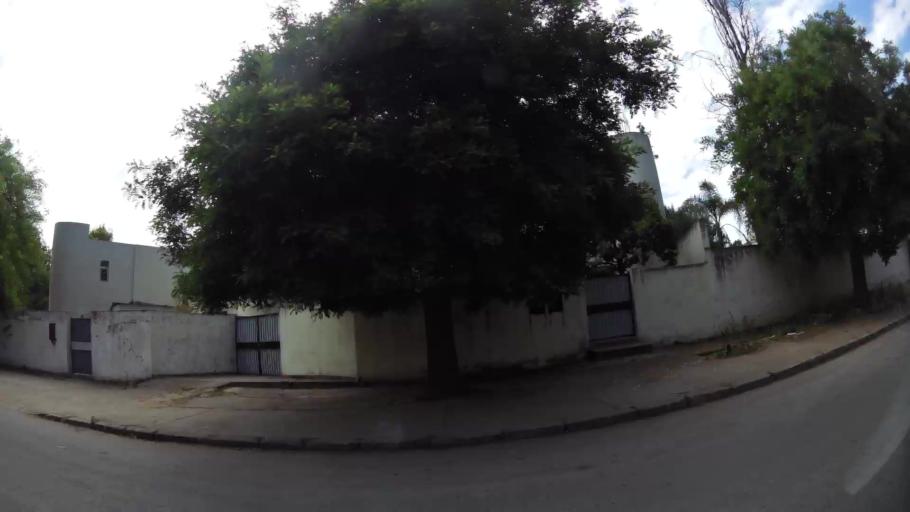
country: MA
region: Gharb-Chrarda-Beni Hssen
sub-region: Kenitra Province
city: Kenitra
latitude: 34.2532
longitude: -6.5905
